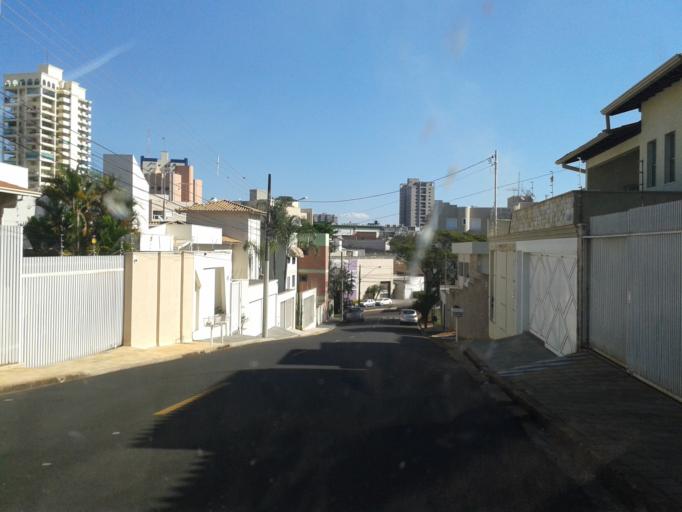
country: BR
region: Minas Gerais
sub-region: Uberaba
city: Uberaba
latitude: -19.7518
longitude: -47.9496
